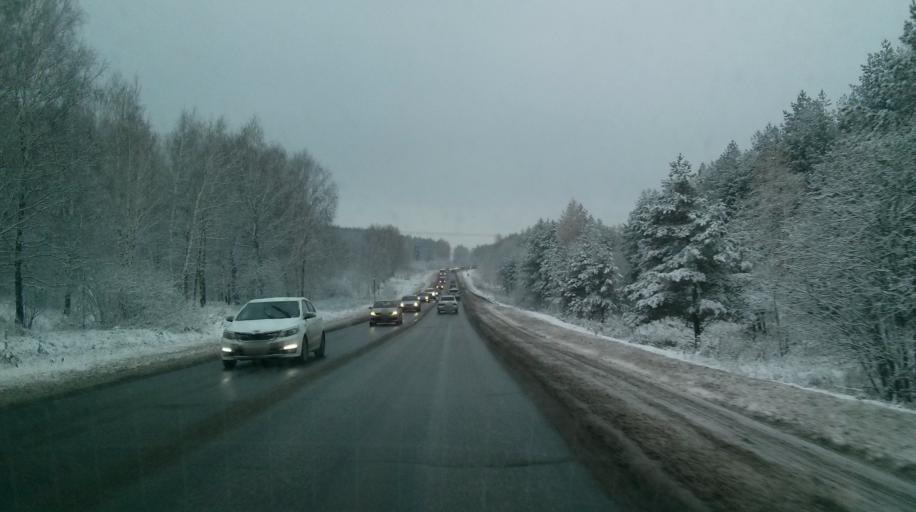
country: RU
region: Nizjnij Novgorod
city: Burevestnik
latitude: 56.1495
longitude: 43.6905
